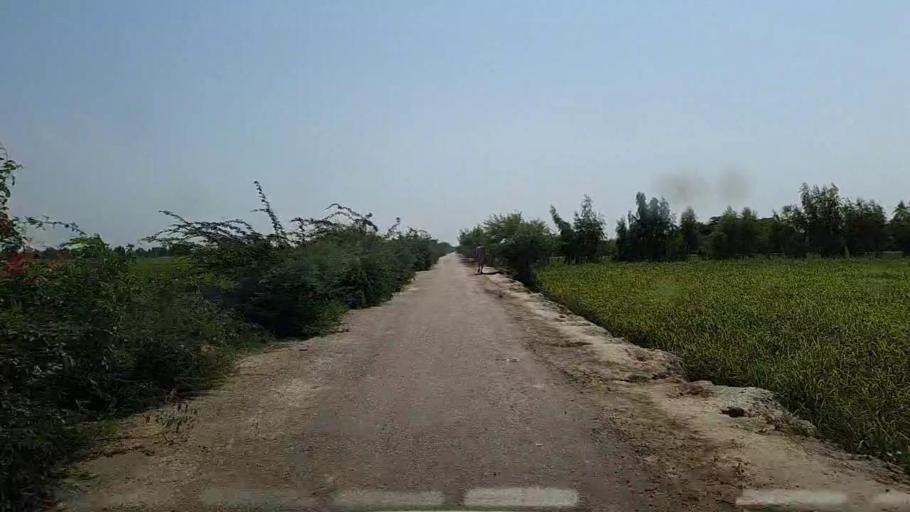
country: PK
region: Sindh
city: Mirpur Batoro
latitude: 24.6163
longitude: 68.4522
